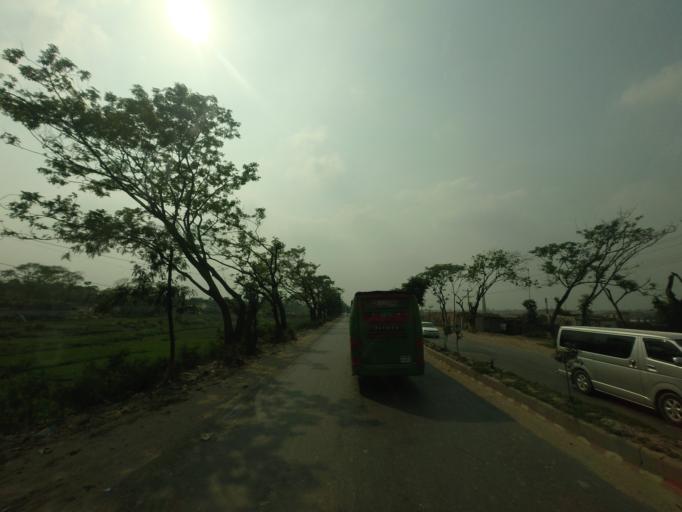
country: BD
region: Dhaka
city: Azimpur
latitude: 23.7914
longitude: 90.3064
